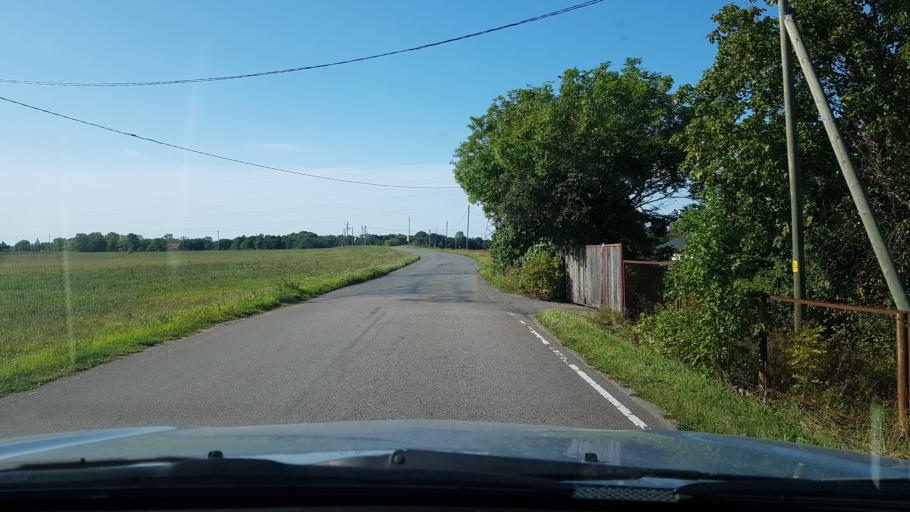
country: EE
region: Ida-Virumaa
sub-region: Narva-Joesuu linn
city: Narva-Joesuu
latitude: 59.4073
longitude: 28.0303
